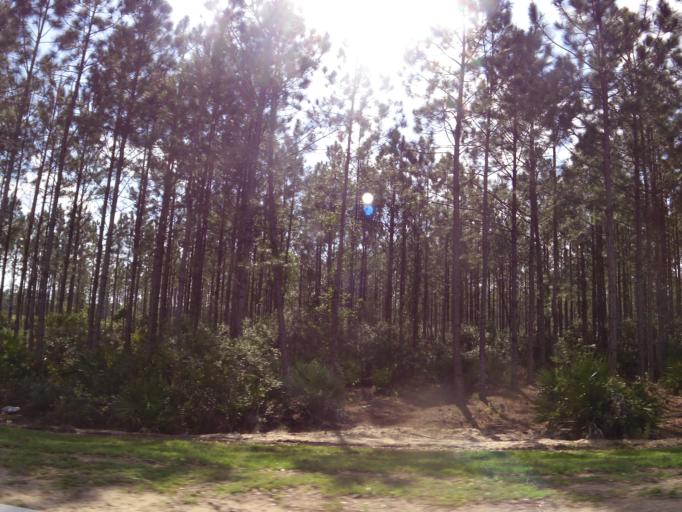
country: US
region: Florida
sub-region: Saint Johns County
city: Palm Valley
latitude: 30.1948
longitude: -81.5069
